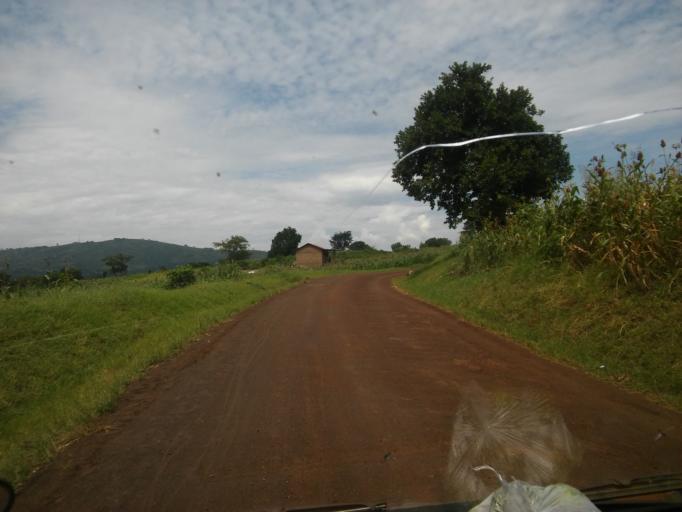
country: UG
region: Eastern Region
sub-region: Manafwa District
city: Manafwa
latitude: 0.8399
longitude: 34.2827
